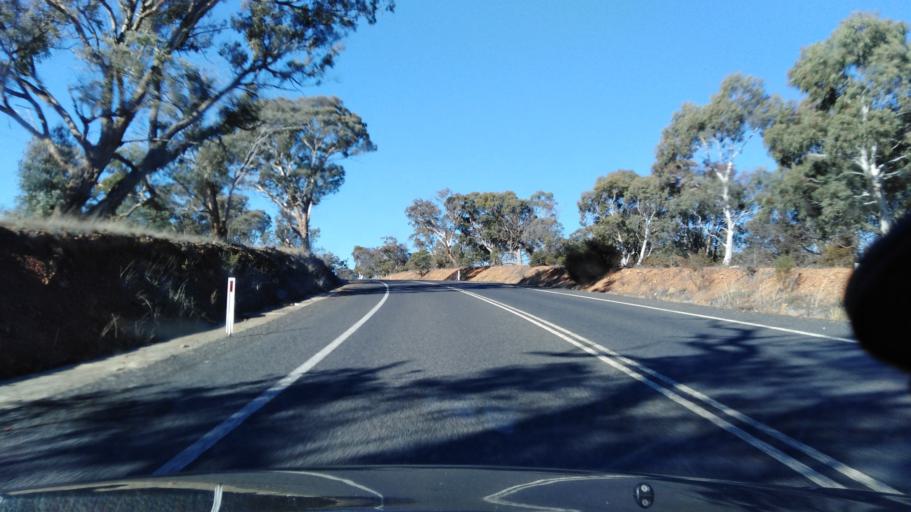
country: AU
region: New South Wales
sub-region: Yass Valley
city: Gundaroo
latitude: -35.1815
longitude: 149.2734
